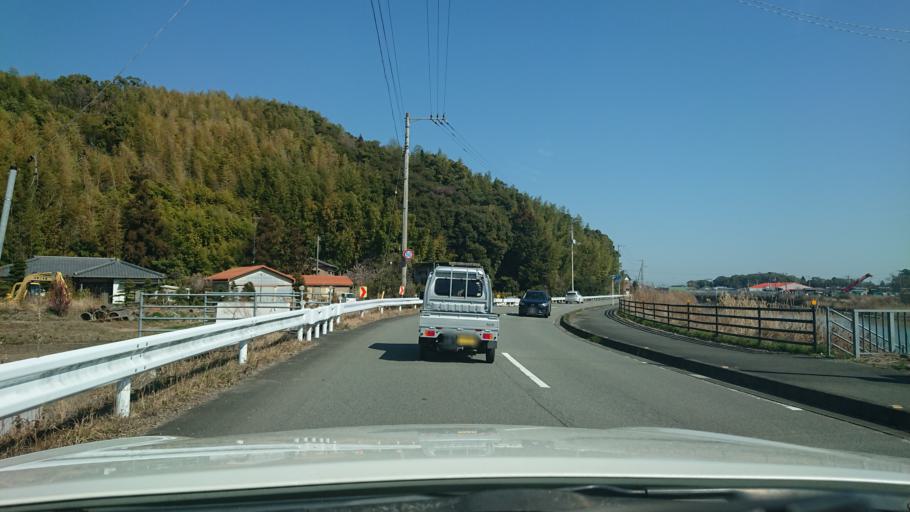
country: JP
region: Tokushima
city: Komatsushimacho
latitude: 33.9717
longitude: 134.5998
